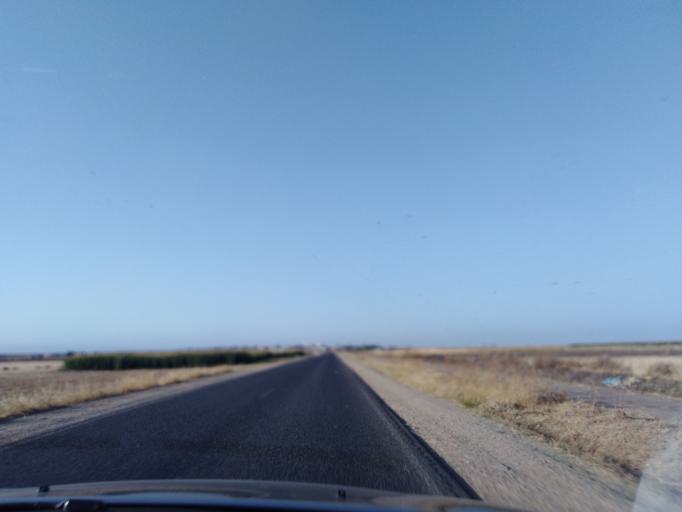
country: MA
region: Doukkala-Abda
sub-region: Safi
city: Safi
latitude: 32.5186
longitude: -8.9115
